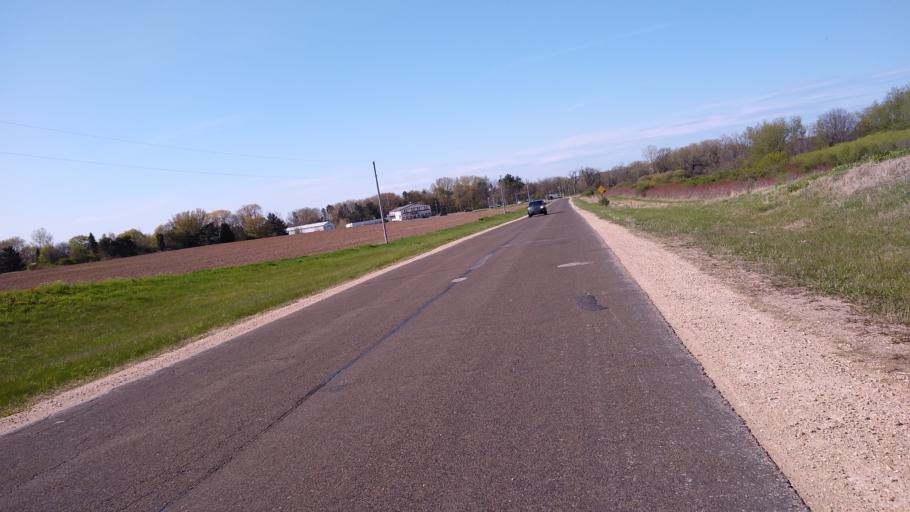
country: US
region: Wisconsin
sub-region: Dane County
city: Waunakee
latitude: 43.1428
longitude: -89.4383
